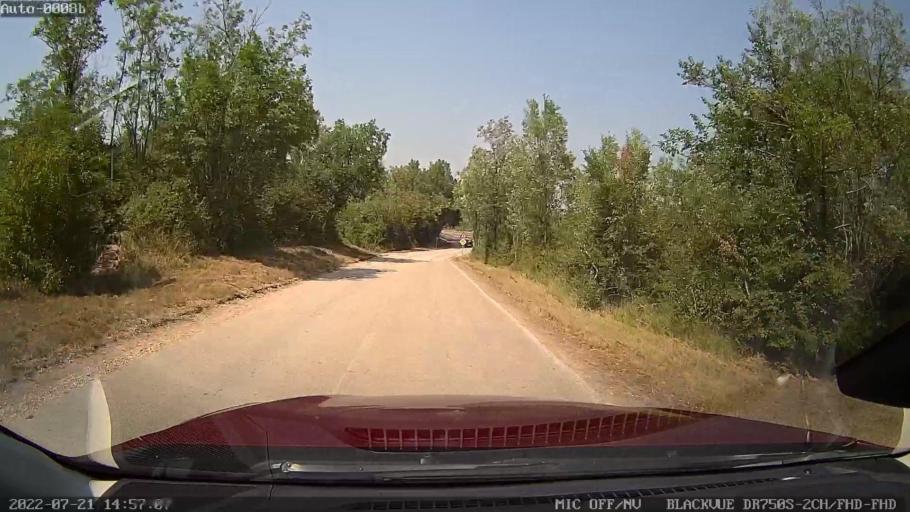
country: HR
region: Istarska
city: Pazin
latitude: 45.2064
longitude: 13.9515
